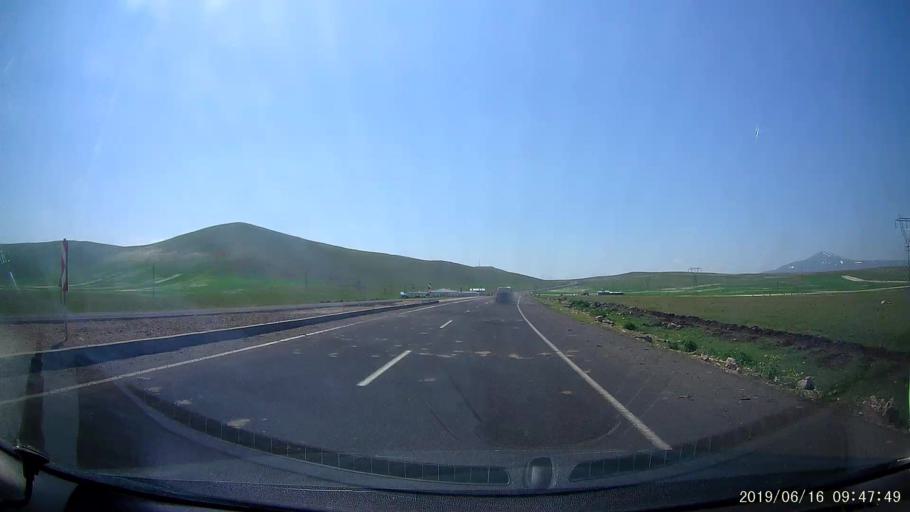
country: TR
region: Kars
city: Digor
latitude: 40.4408
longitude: 43.3482
